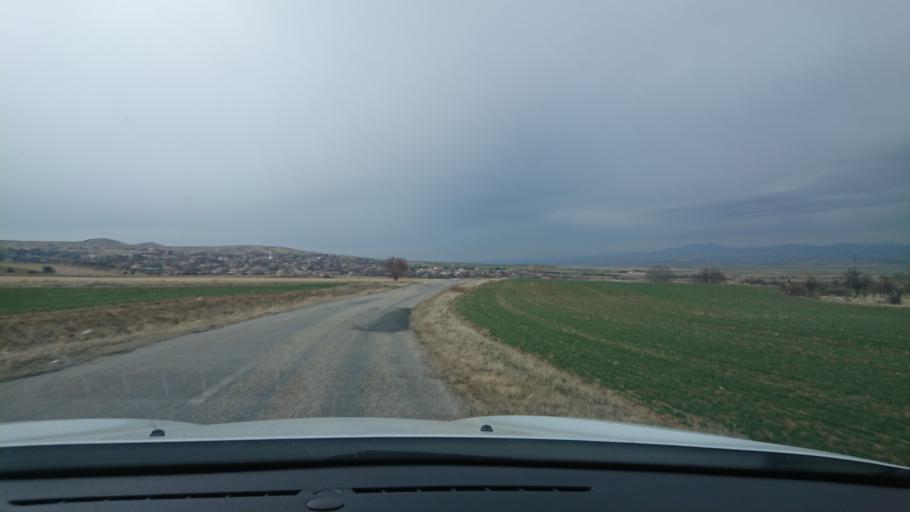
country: TR
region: Aksaray
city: Sariyahsi
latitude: 38.9522
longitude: 33.8994
